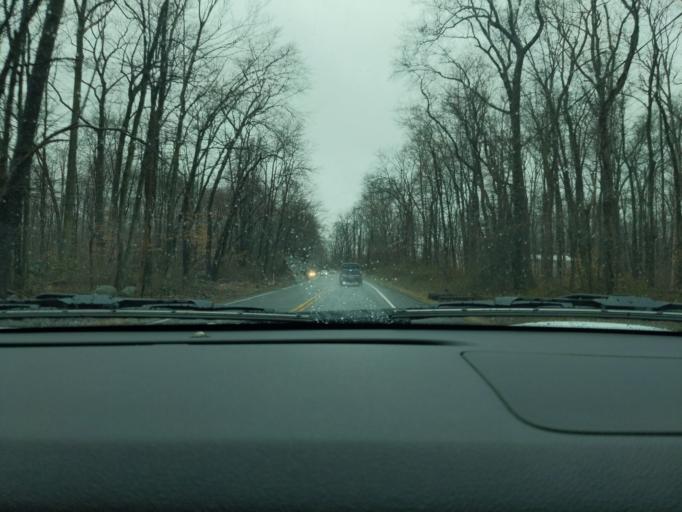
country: US
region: Pennsylvania
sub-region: Bucks County
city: Perkasie
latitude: 40.4252
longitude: -75.2826
